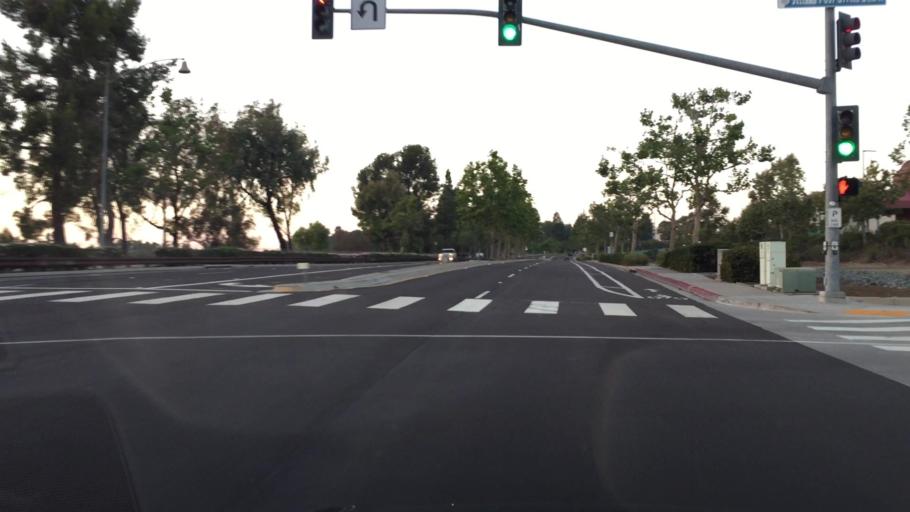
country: US
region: California
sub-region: San Diego County
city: Poway
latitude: 32.9825
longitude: -117.0828
